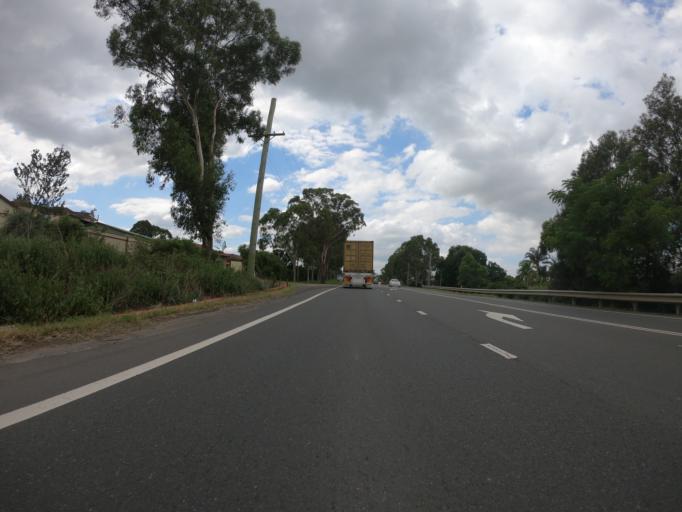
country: AU
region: New South Wales
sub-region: Blacktown
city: Mount Druitt
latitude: -33.8106
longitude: 150.7870
